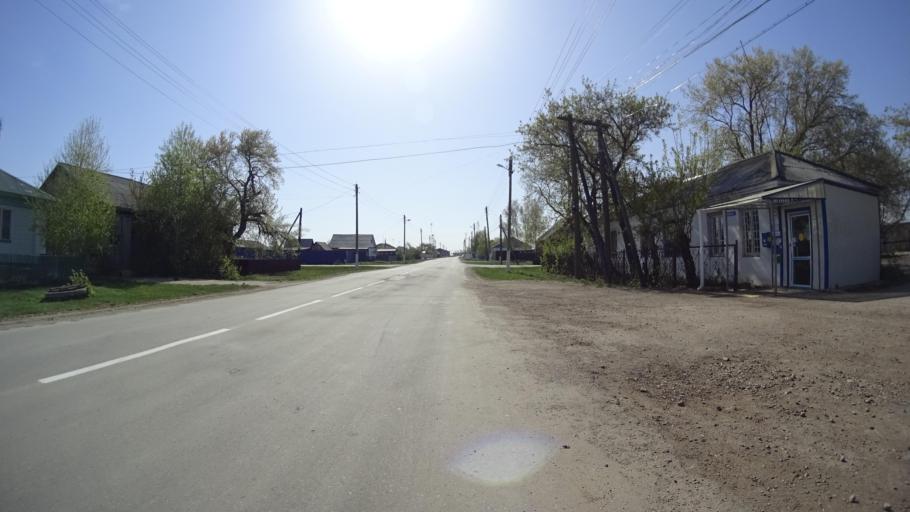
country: RU
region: Chelyabinsk
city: Chesma
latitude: 53.7974
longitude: 61.0289
